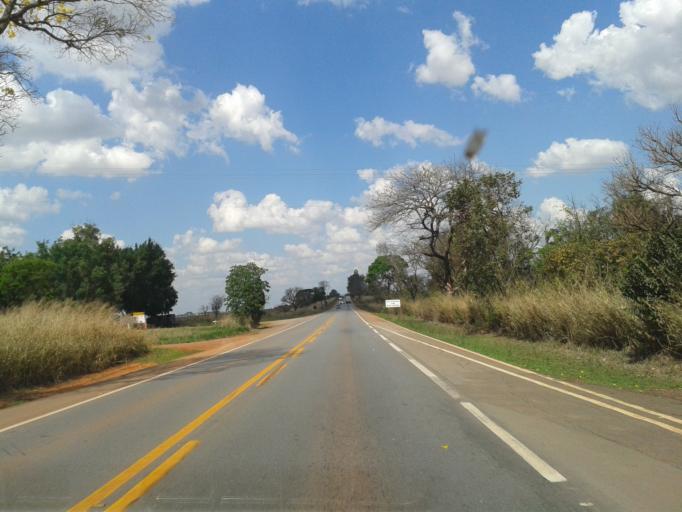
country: BR
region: Minas Gerais
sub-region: Luz
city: Luz
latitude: -19.7820
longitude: -45.7276
